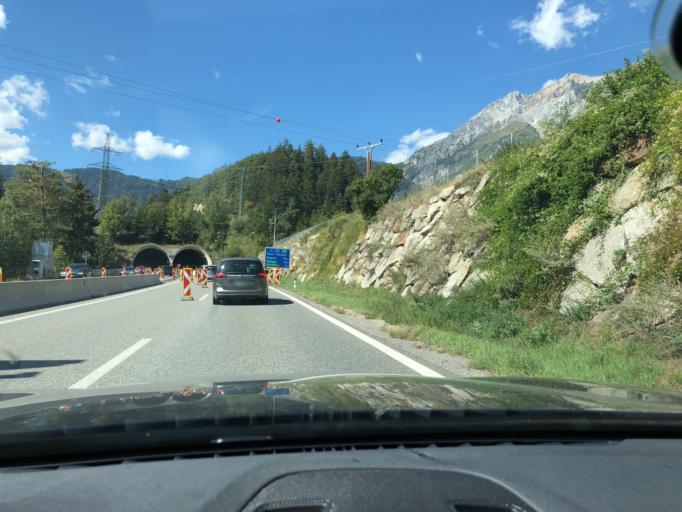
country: AT
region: Tyrol
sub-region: Politischer Bezirk Landeck
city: Grins
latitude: 47.1384
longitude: 10.5303
